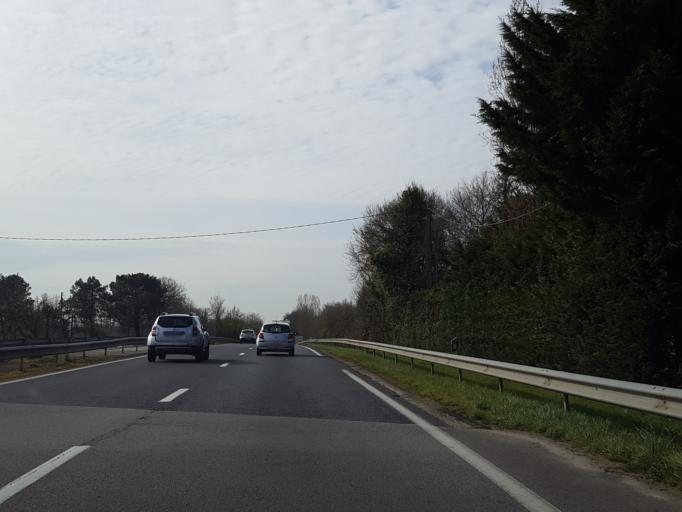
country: FR
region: Pays de la Loire
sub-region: Departement de la Vendee
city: Belleville-sur-Vie
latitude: 46.7671
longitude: -1.4310
